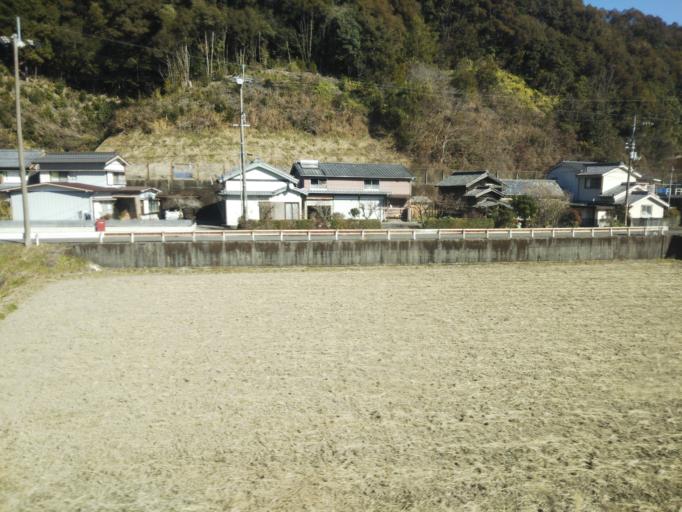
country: JP
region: Kochi
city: Nakamura
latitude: 33.1016
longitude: 133.0990
